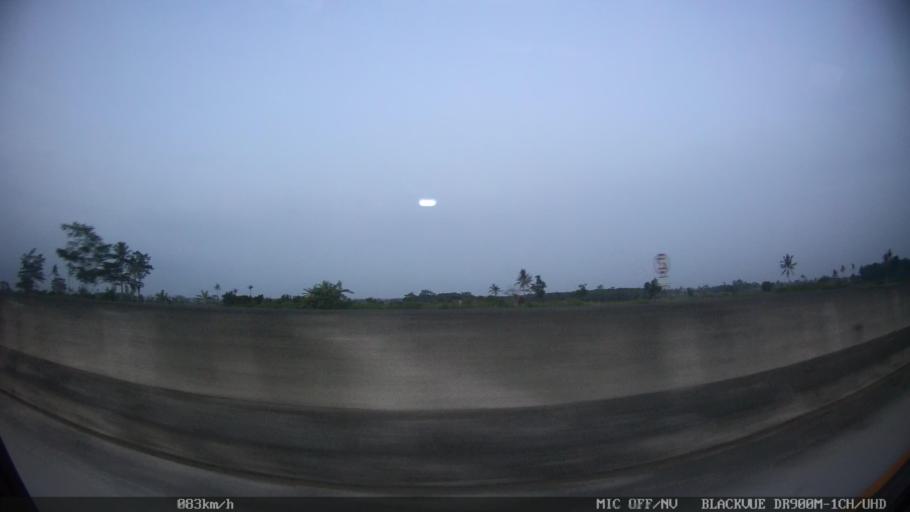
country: ID
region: Lampung
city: Sidorejo
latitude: -5.6171
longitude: 105.5609
